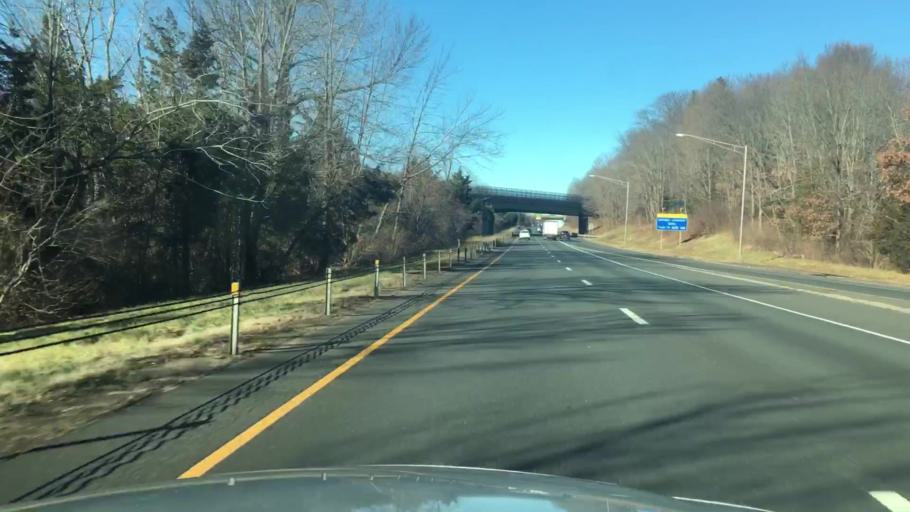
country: US
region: Connecticut
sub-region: Middlesex County
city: Cromwell
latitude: 41.6070
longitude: -72.6752
